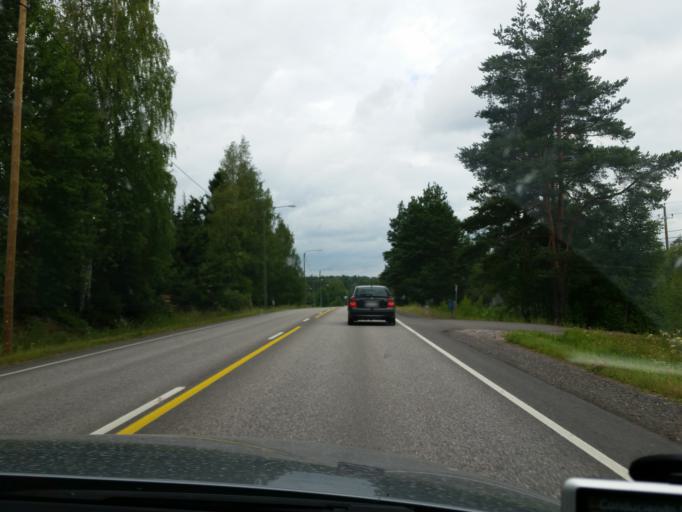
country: FI
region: Uusimaa
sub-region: Helsinki
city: Vihti
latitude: 60.3504
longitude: 24.1875
